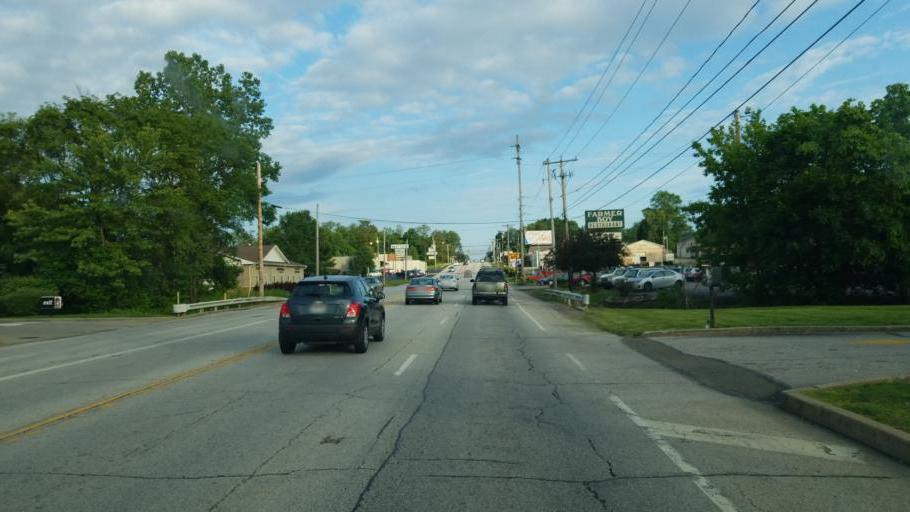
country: US
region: Ohio
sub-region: Summit County
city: Lakemore
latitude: 41.0304
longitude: -81.4268
